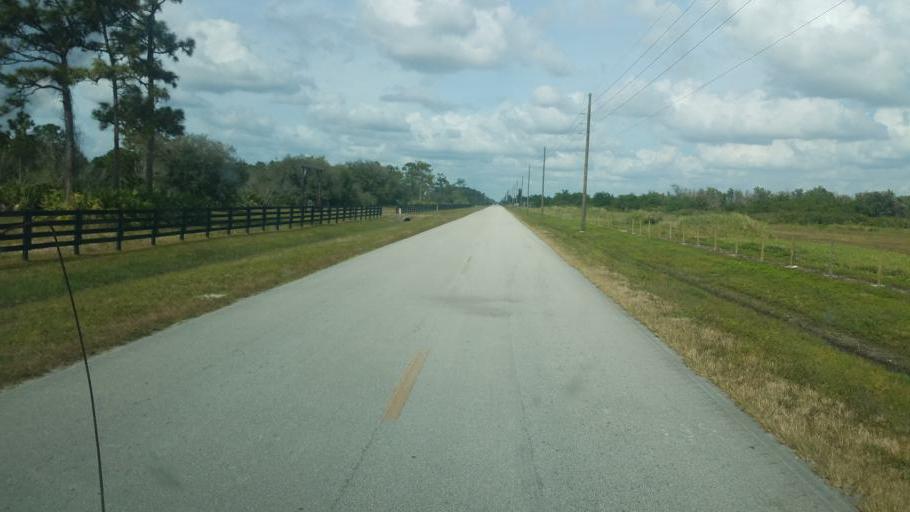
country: US
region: Florida
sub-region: Okeechobee County
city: Cypress Quarters
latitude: 27.4744
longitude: -80.7714
